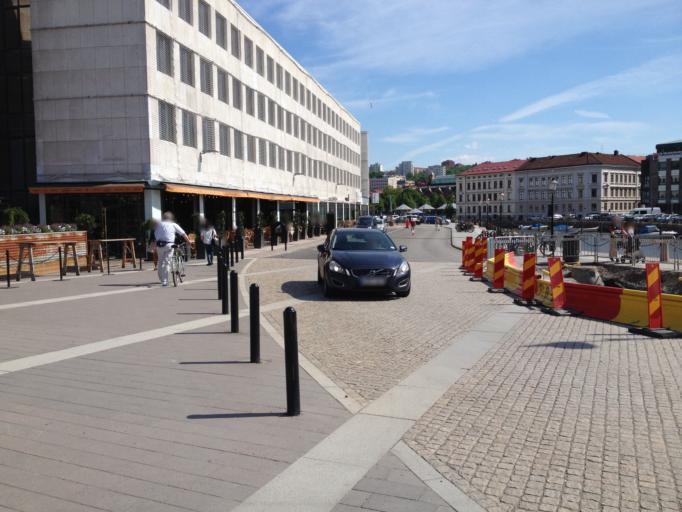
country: SE
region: Vaestra Goetaland
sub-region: Goteborg
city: Goeteborg
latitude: 57.7021
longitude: 11.9553
